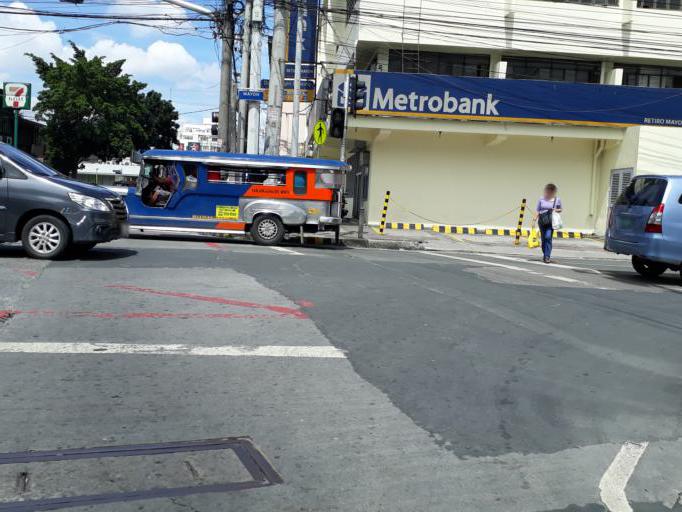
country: PH
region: Calabarzon
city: Del Monte
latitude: 14.6298
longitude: 120.9957
